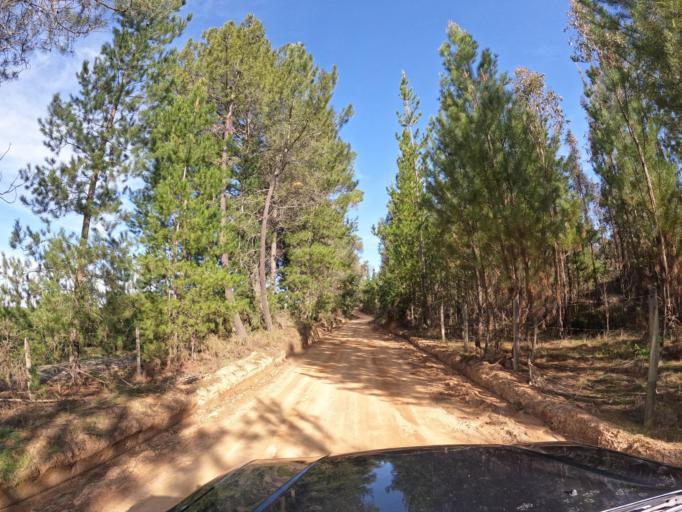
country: CL
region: Biobio
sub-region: Provincia de Biobio
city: La Laja
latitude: -37.1211
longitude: -72.7370
